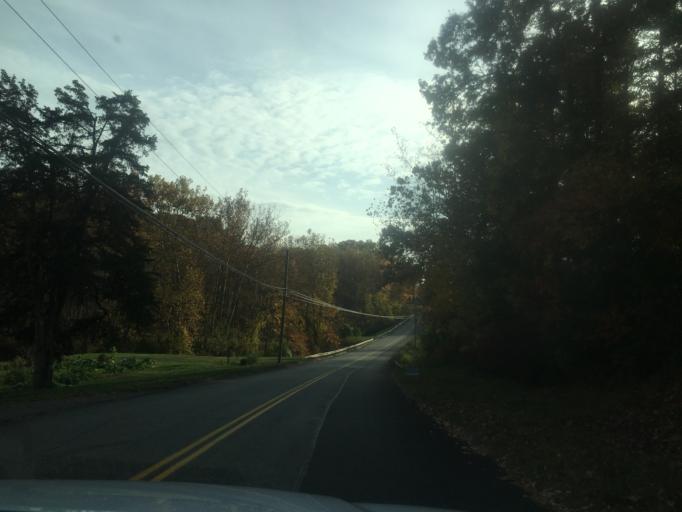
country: US
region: Connecticut
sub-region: Hartford County
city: Broad Brook
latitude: 41.8805
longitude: -72.5742
